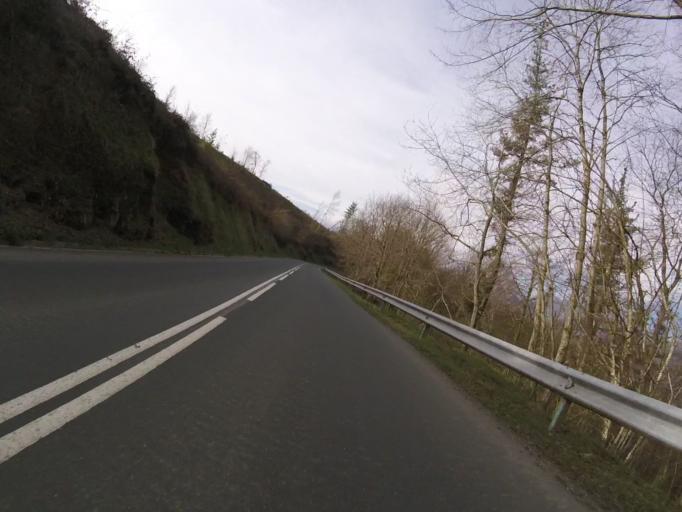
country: ES
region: Basque Country
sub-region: Provincia de Guipuzcoa
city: Beizama
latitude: 43.1650
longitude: -2.2154
